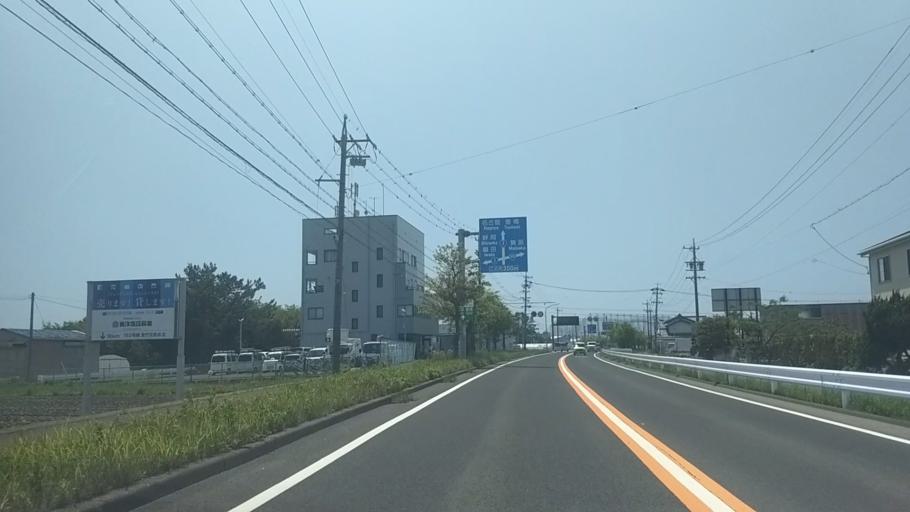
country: JP
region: Shizuoka
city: Hamamatsu
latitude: 34.6824
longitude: 137.6669
